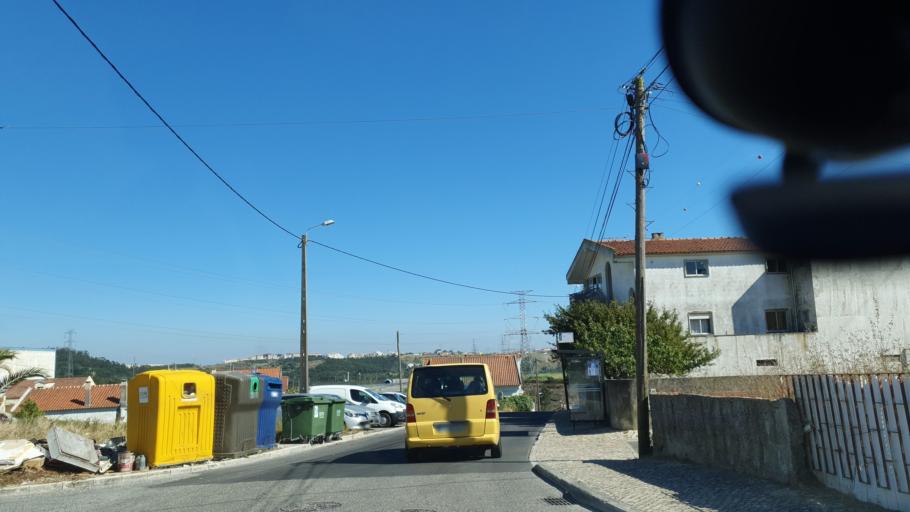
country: PT
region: Lisbon
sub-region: Sintra
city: Belas
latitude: 38.7985
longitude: -9.2499
